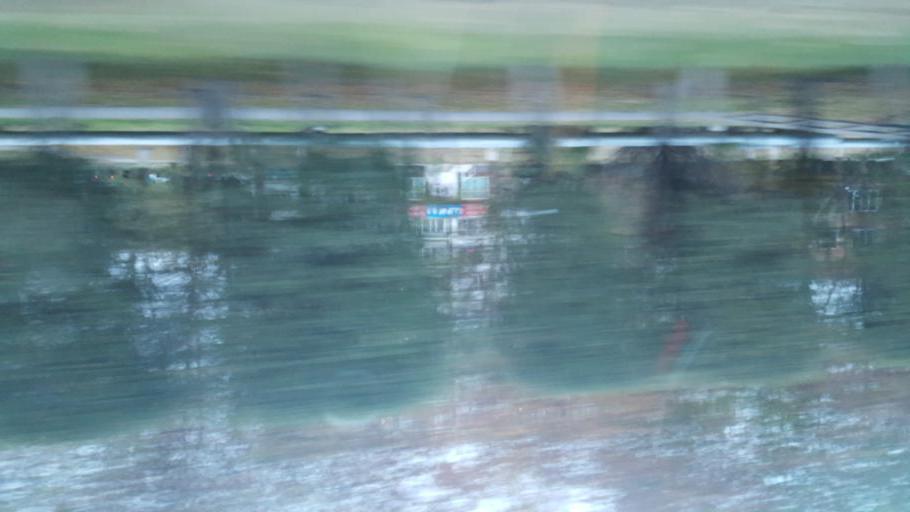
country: KZ
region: Astana Qalasy
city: Astana
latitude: 51.1531
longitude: 71.4900
